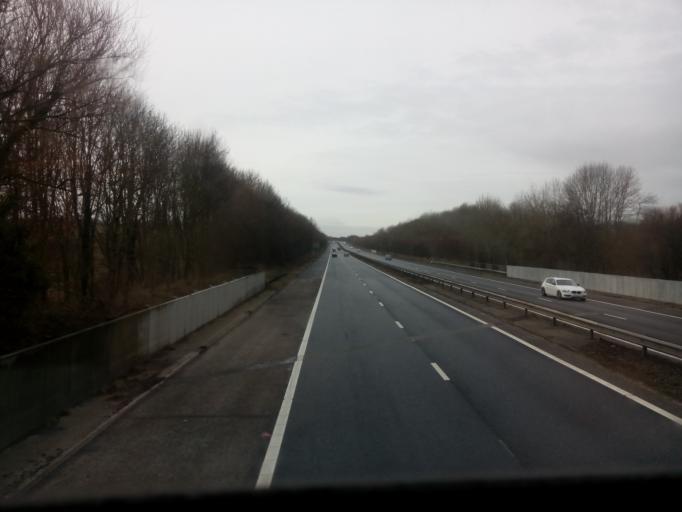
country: GB
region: England
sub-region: Hampshire
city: Kings Worthy
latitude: 51.0903
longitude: -1.2820
